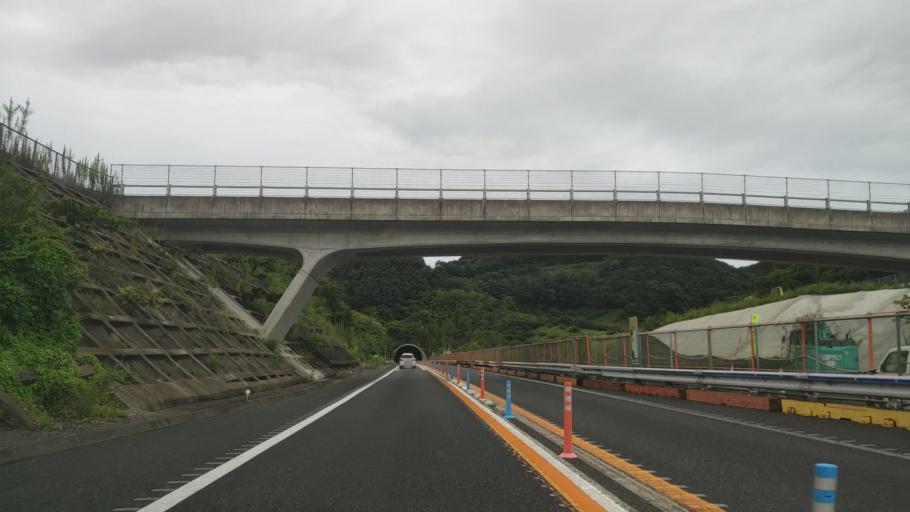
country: JP
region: Wakayama
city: Tanabe
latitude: 33.7842
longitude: 135.3141
